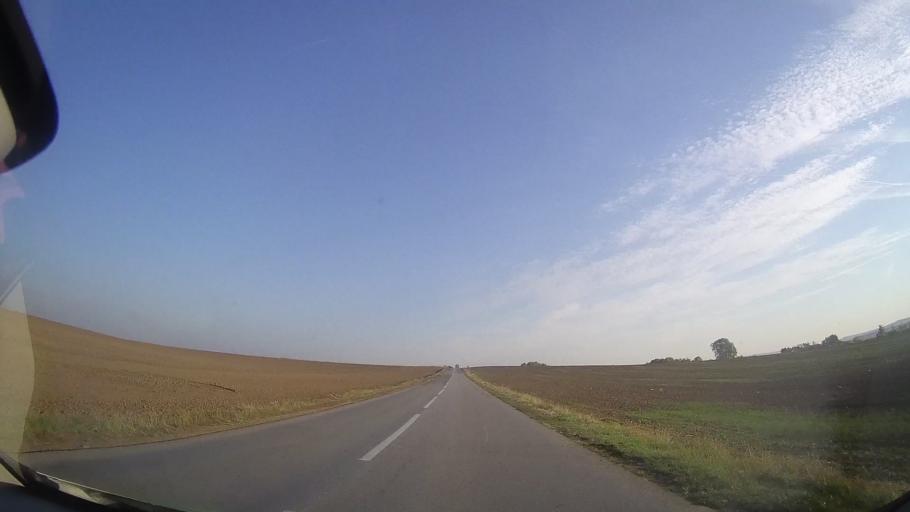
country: RO
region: Timis
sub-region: Comuna Fibis
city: Fibis
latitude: 45.9406
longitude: 21.4017
